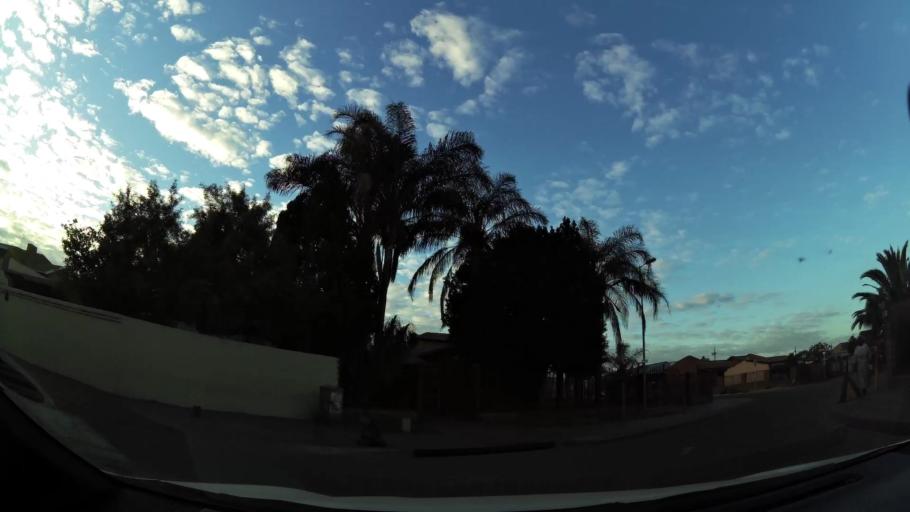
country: ZA
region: Gauteng
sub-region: City of Tshwane Metropolitan Municipality
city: Pretoria
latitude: -25.7170
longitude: 28.3488
